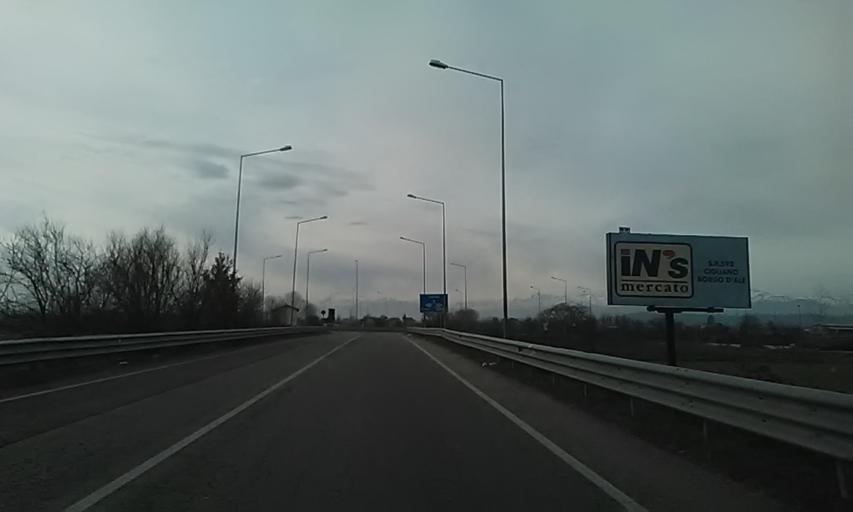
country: IT
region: Piedmont
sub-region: Provincia di Vercelli
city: Cigliano
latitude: 45.2973
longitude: 8.0244
